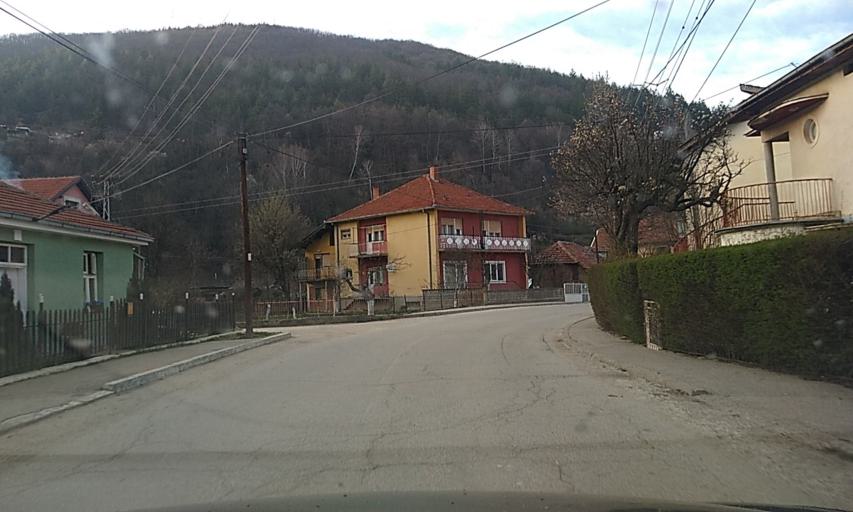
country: RS
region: Central Serbia
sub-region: Pcinjski Okrug
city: Bosilegrad
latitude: 42.4984
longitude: 22.4690
